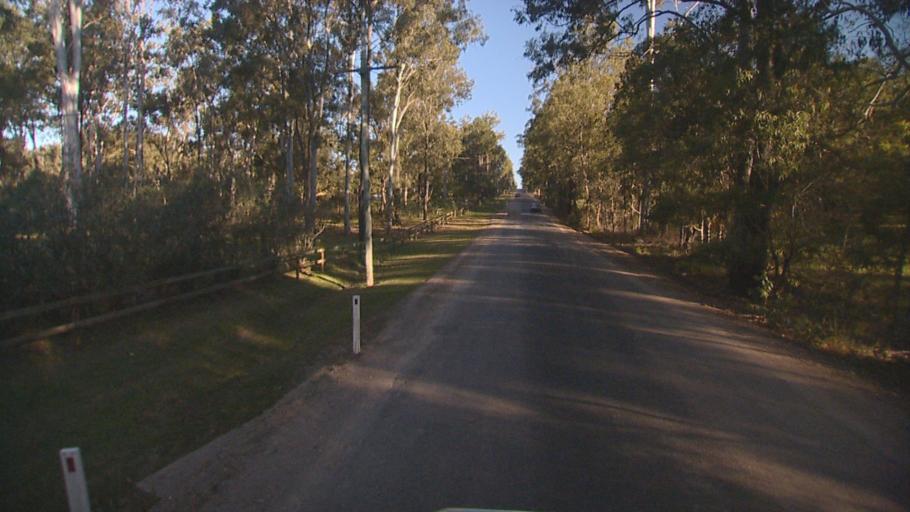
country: AU
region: Queensland
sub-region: Logan
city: Chambers Flat
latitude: -27.7726
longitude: 153.1371
